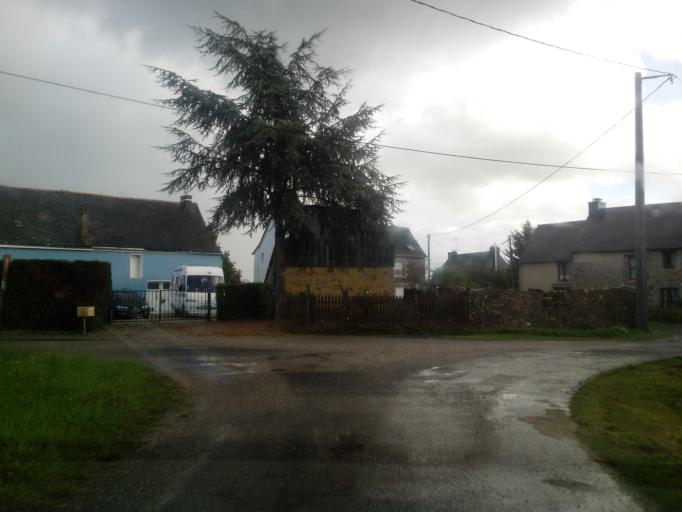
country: FR
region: Brittany
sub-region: Departement du Morbihan
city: Mauron
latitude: 48.0851
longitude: -2.3390
